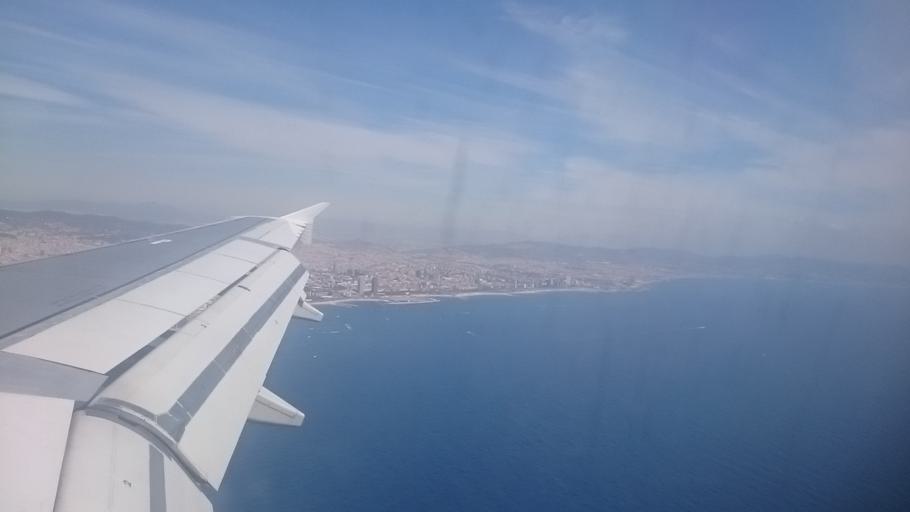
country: ES
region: Catalonia
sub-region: Provincia de Barcelona
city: Ciutat Vella
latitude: 41.3409
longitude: 2.2052
